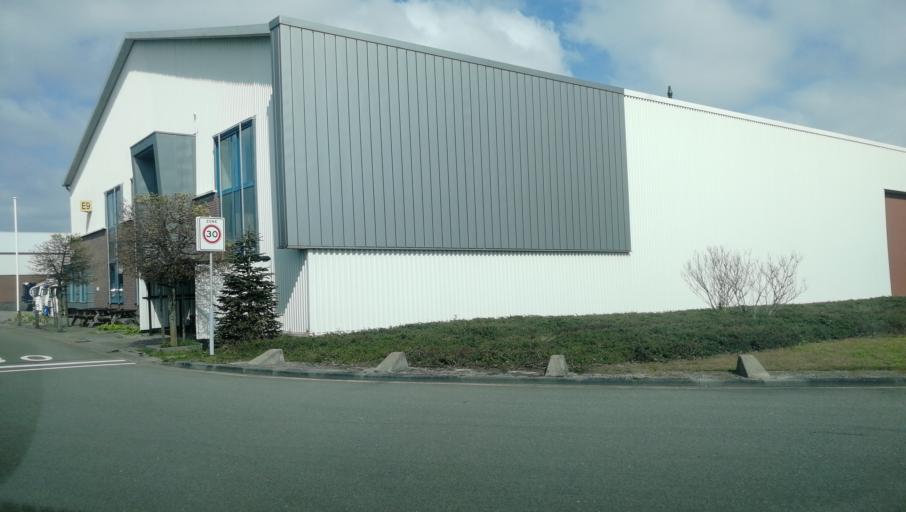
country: NL
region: Limburg
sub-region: Gemeente Venlo
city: Venlo
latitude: 51.4031
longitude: 6.1365
